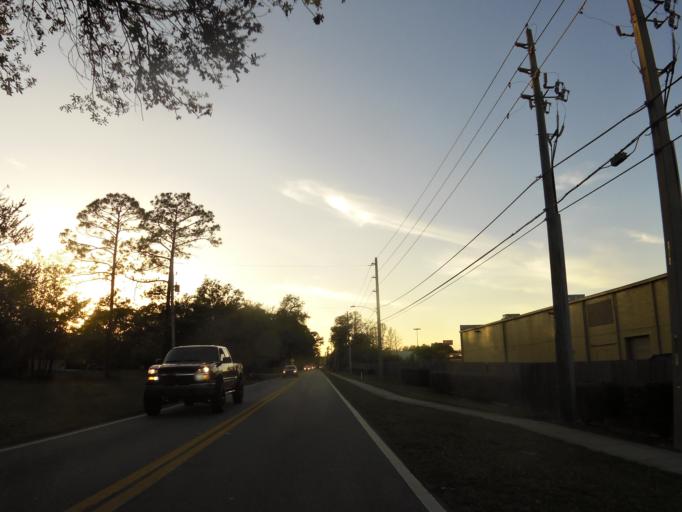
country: US
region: Florida
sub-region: Duval County
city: Jacksonville
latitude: 30.2868
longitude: -81.5809
